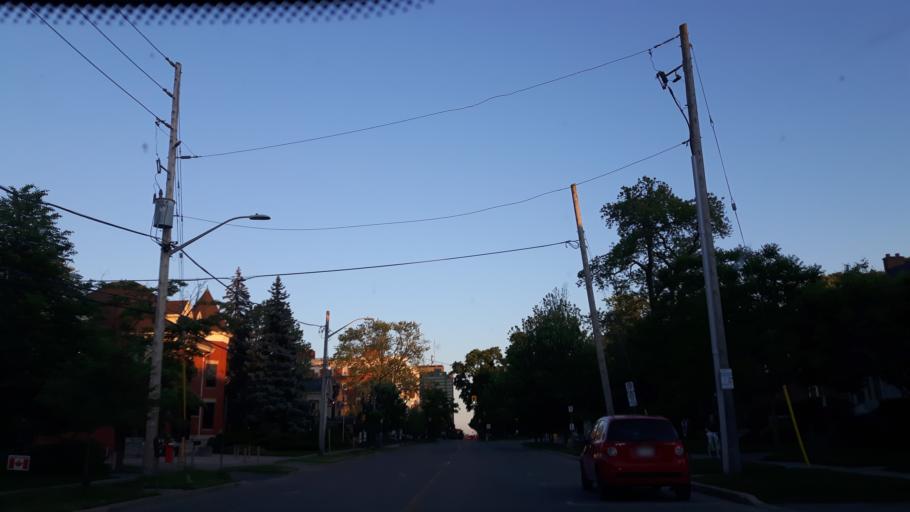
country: CA
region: Ontario
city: London
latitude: 42.9918
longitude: -81.2488
